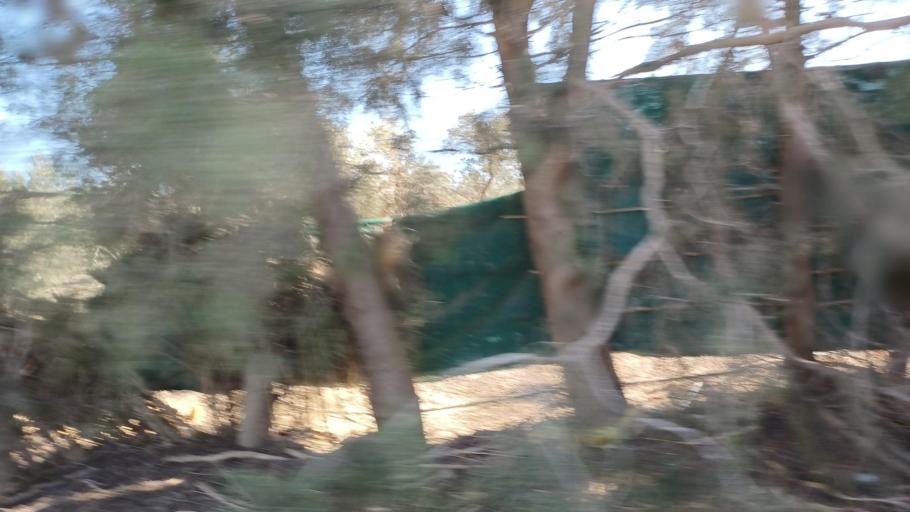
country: CY
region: Larnaka
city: Voroklini
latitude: 34.9973
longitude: 33.6718
